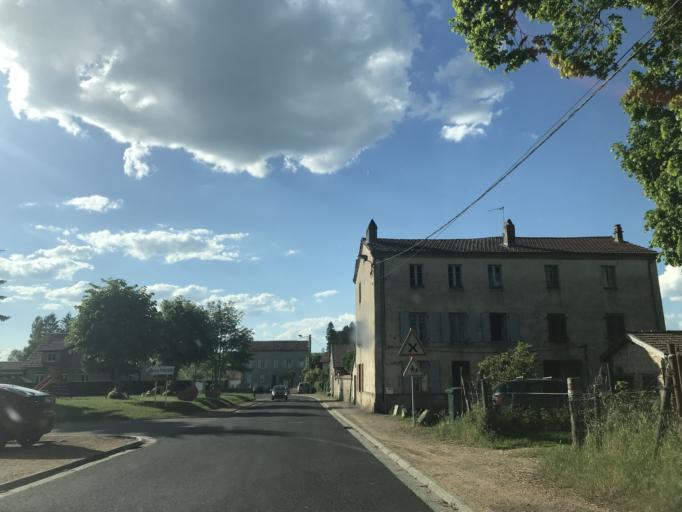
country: FR
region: Auvergne
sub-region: Departement du Puy-de-Dome
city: Job
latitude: 45.6191
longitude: 3.6800
